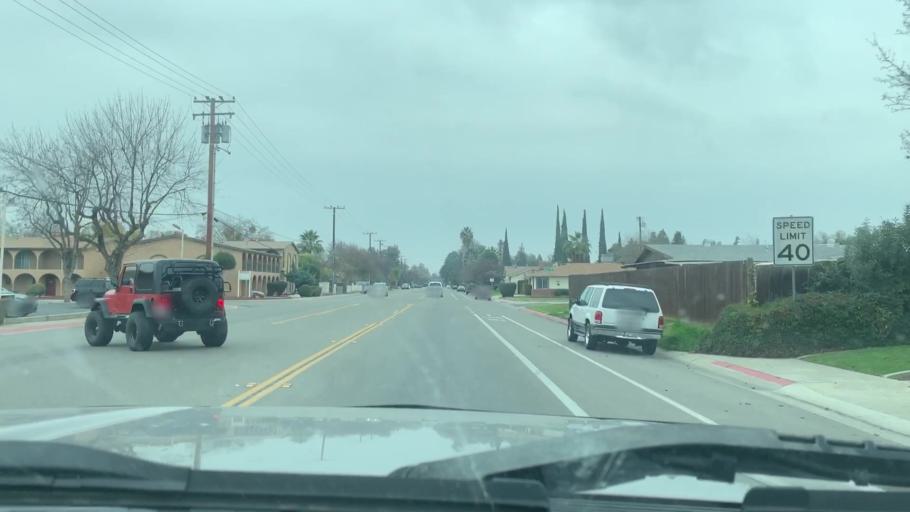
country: US
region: California
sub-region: Tulare County
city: Visalia
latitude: 36.3133
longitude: -119.3053
